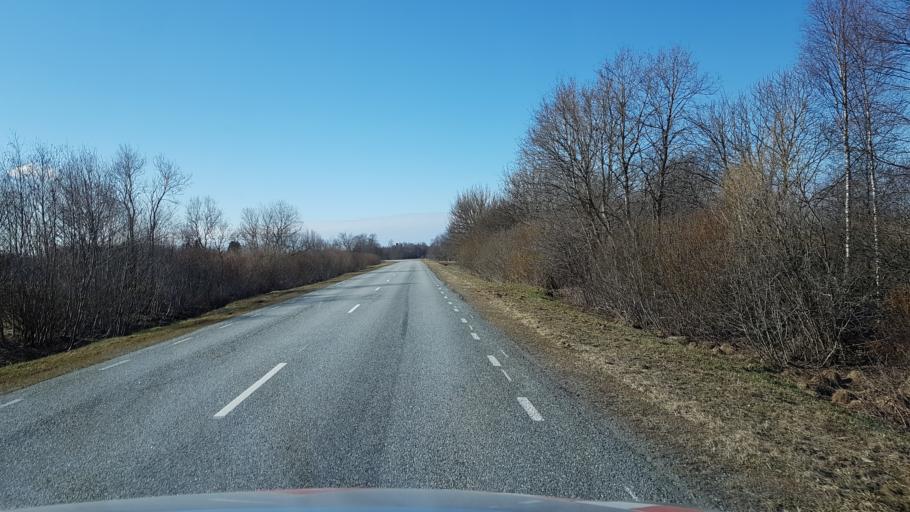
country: EE
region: Laeaene-Virumaa
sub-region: Haljala vald
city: Haljala
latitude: 59.4975
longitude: 26.1370
